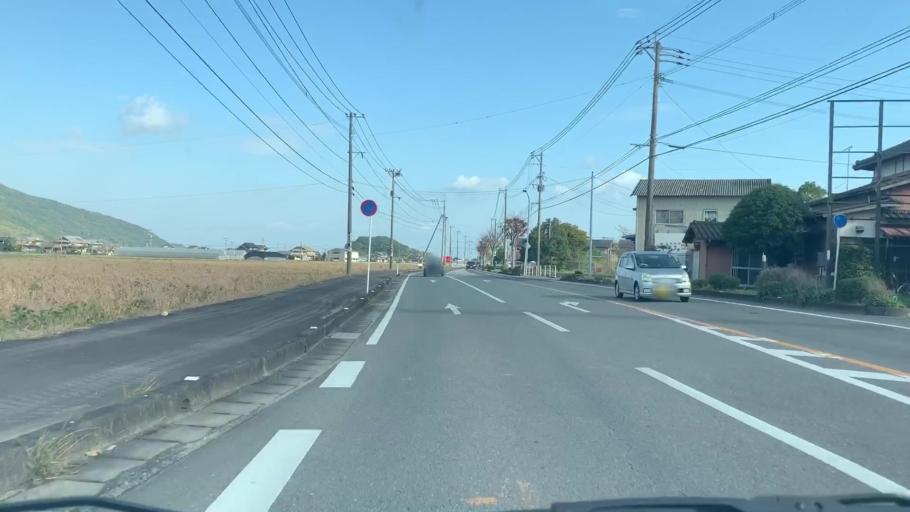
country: JP
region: Saga Prefecture
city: Kashima
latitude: 33.1244
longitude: 130.0726
